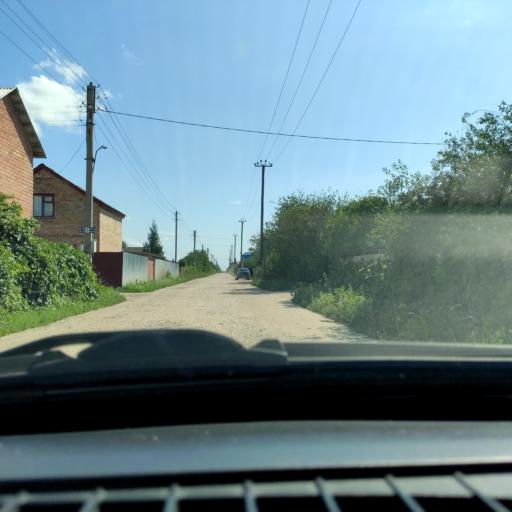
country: RU
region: Samara
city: Tol'yatti
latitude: 53.7311
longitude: 49.3956
